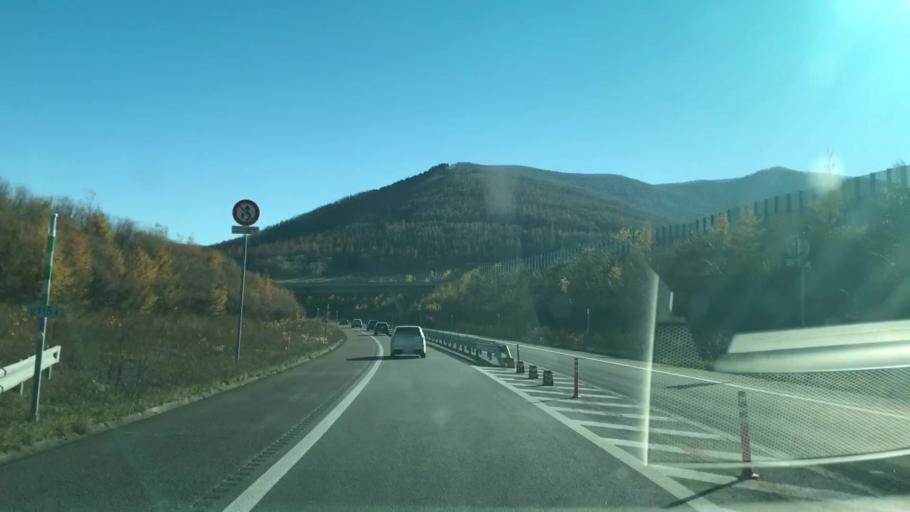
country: JP
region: Hokkaido
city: Otofuke
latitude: 43.0428
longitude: 142.7836
